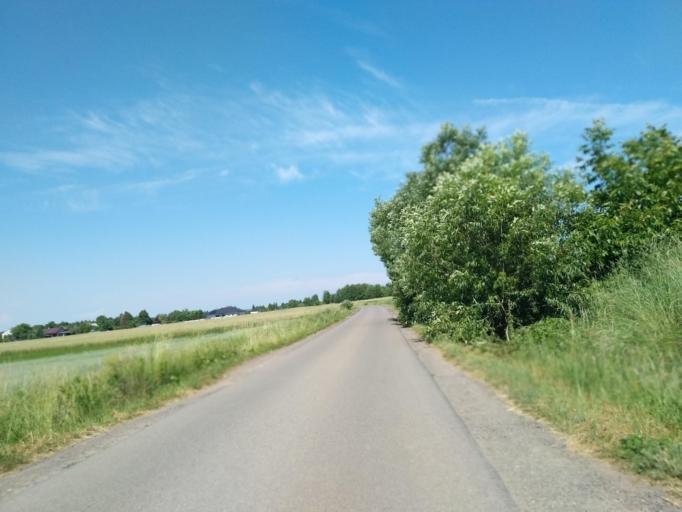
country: PL
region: Subcarpathian Voivodeship
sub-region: Powiat krosnienski
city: Korczyna
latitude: 49.7246
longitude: 21.7771
